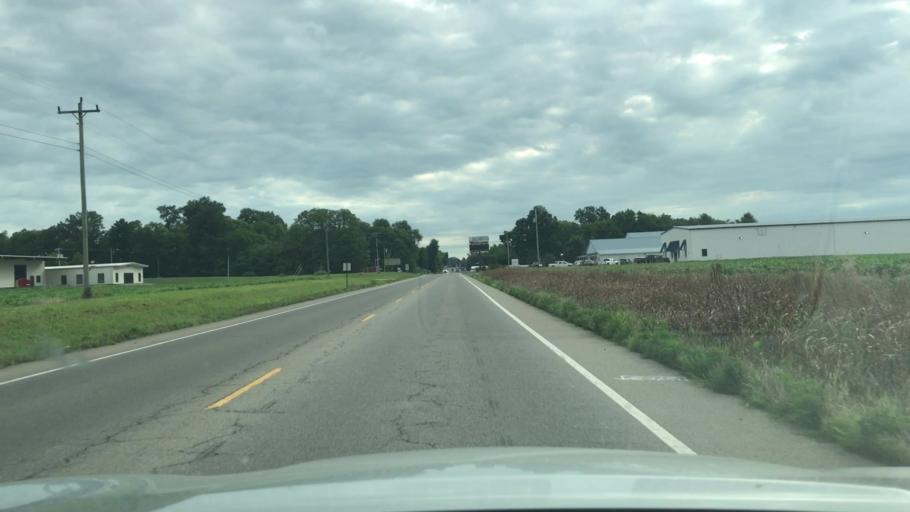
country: US
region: Kentucky
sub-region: Todd County
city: Guthrie
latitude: 36.6391
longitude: -87.2073
